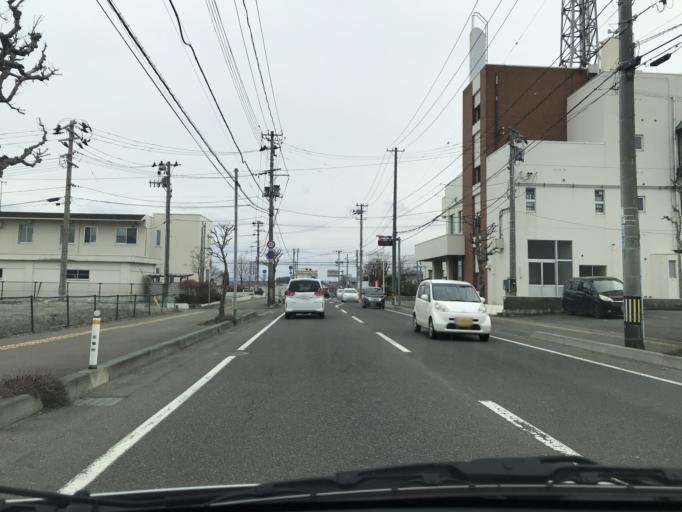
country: JP
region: Iwate
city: Hanamaki
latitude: 39.3868
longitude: 141.1093
